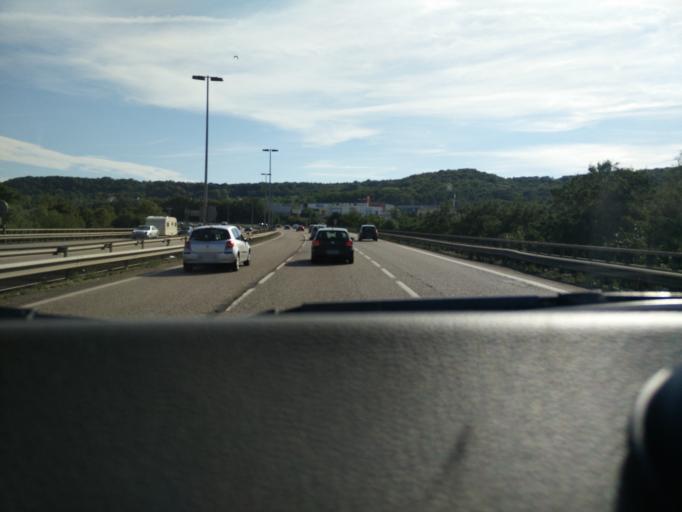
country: FR
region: Lorraine
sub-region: Departement de Meurthe-et-Moselle
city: Champigneulles
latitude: 48.7460
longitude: 6.1539
